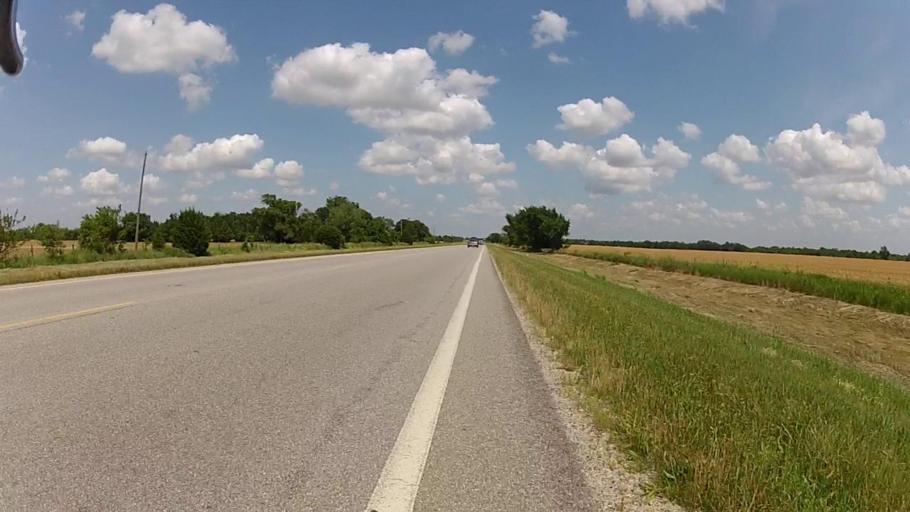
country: US
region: Kansas
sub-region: Labette County
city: Altamont
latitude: 37.1932
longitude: -95.2394
